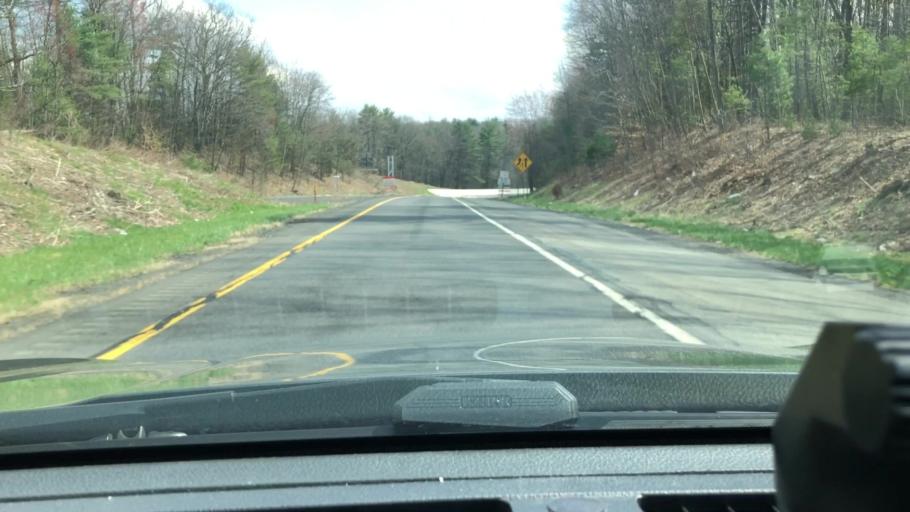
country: US
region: Pennsylvania
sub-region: Monroe County
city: Arlington Heights
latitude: 40.9957
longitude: -75.2709
